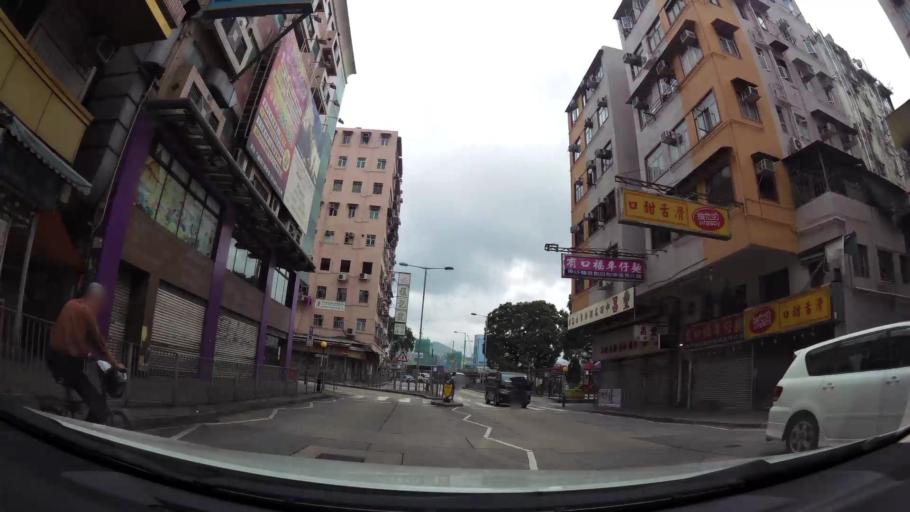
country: HK
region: Kowloon City
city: Kowloon
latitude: 22.3289
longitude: 114.1912
